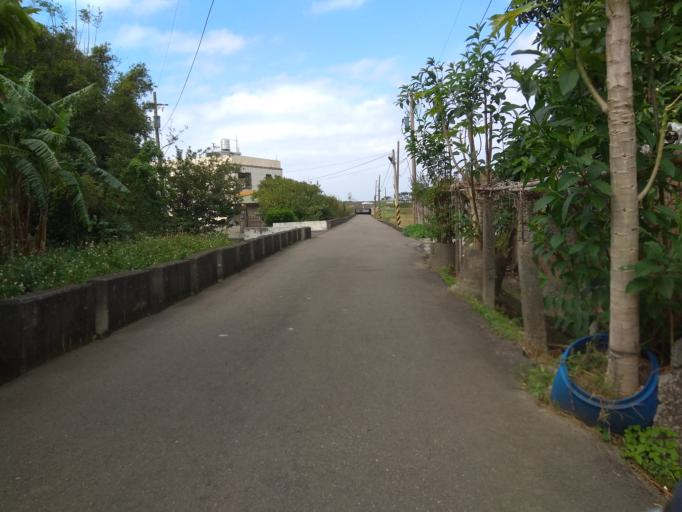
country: TW
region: Taiwan
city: Taoyuan City
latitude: 25.0619
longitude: 121.2160
